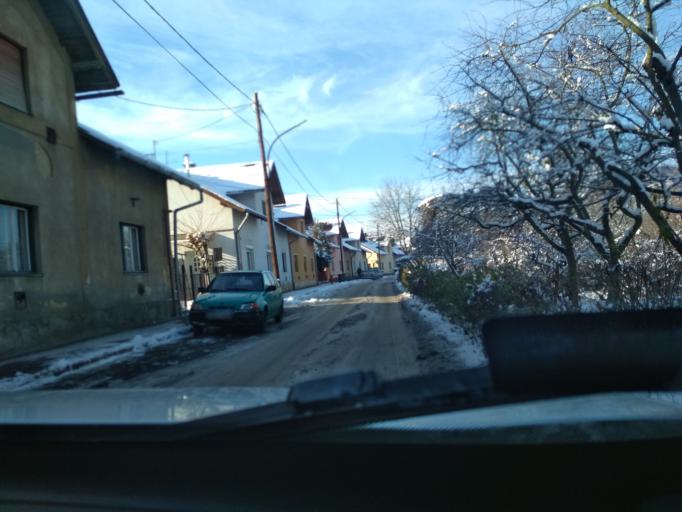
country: HU
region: Nograd
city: Salgotarjan
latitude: 48.1114
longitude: 19.8269
